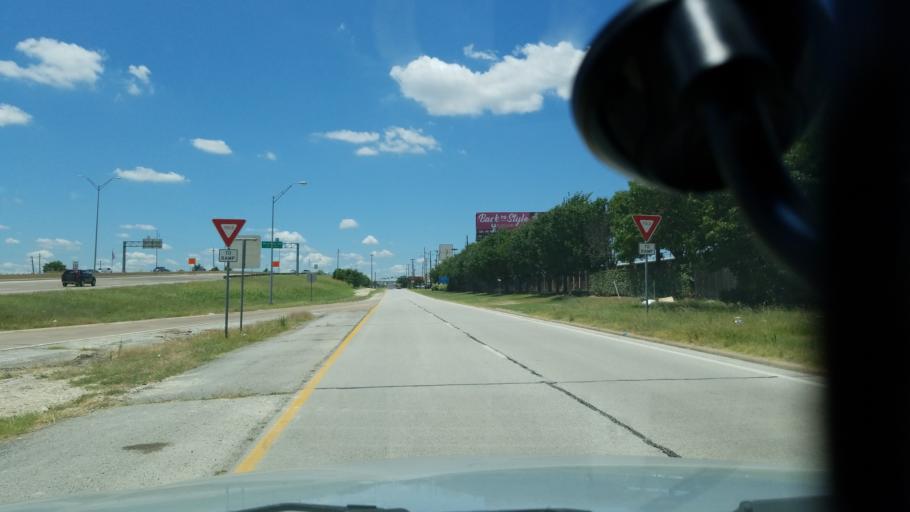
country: US
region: Texas
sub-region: Dallas County
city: Duncanville
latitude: 32.6649
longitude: -96.8681
